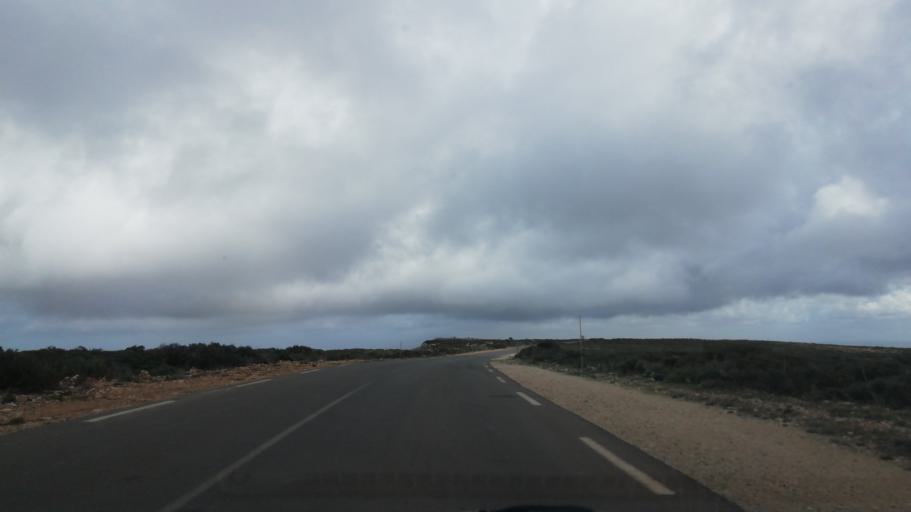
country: DZ
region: Oran
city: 'Ain el Turk
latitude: 35.6992
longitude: -0.7658
